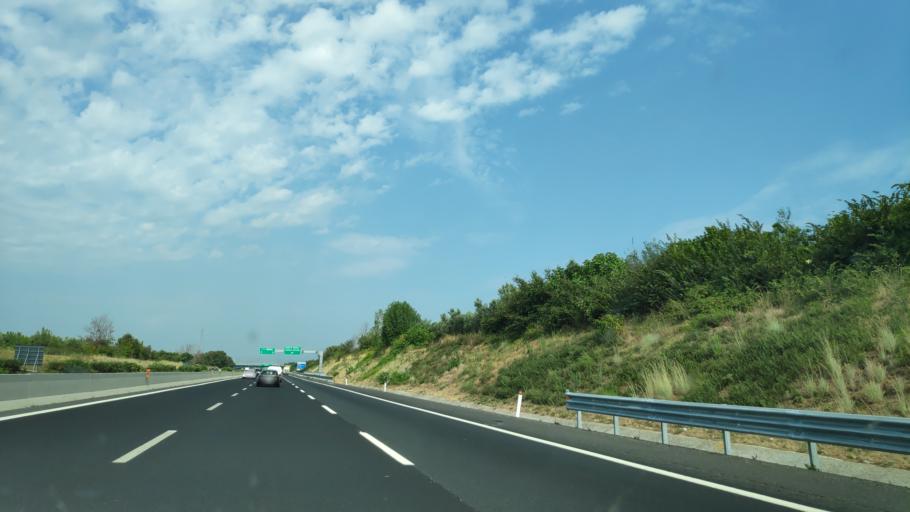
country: IT
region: Campania
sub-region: Provincia di Caserta
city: San Prisco
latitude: 41.1006
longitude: 14.2639
